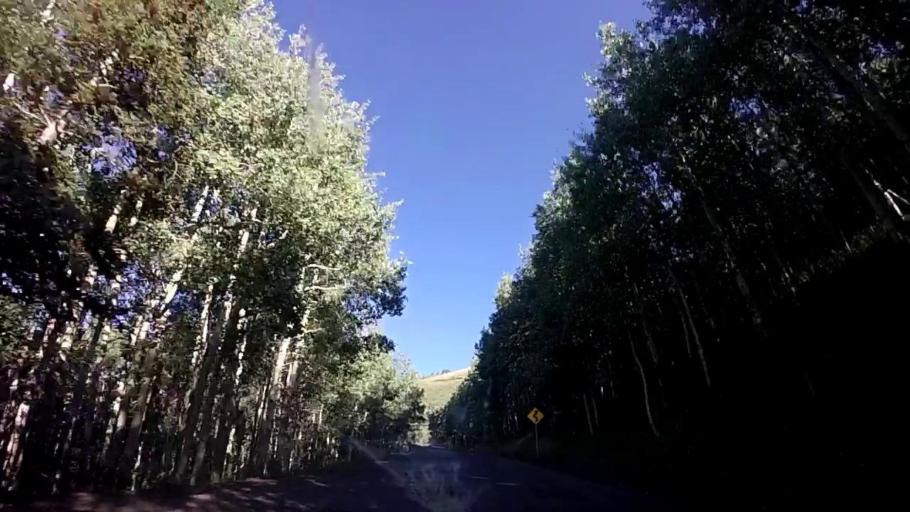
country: US
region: Utah
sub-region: Summit County
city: Park City
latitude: 40.6077
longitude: -111.5270
